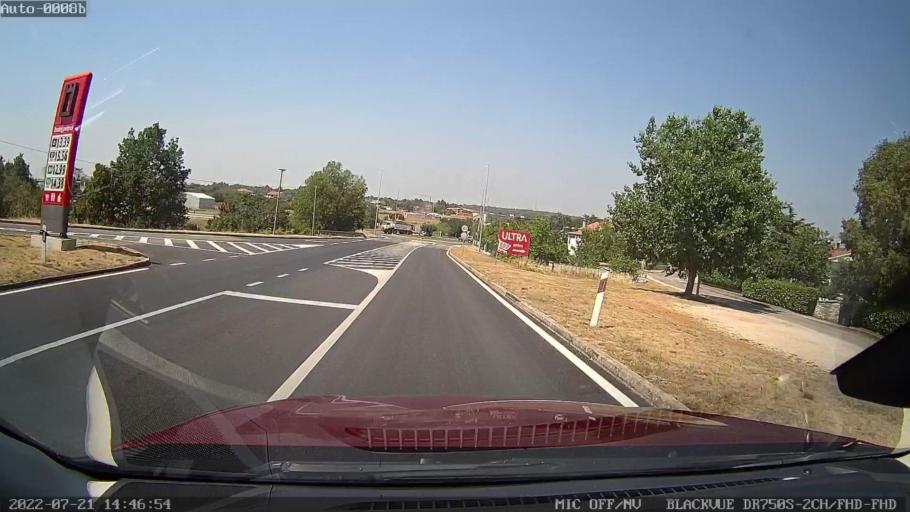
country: HR
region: Istarska
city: Pazin
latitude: 45.1403
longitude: 13.9012
